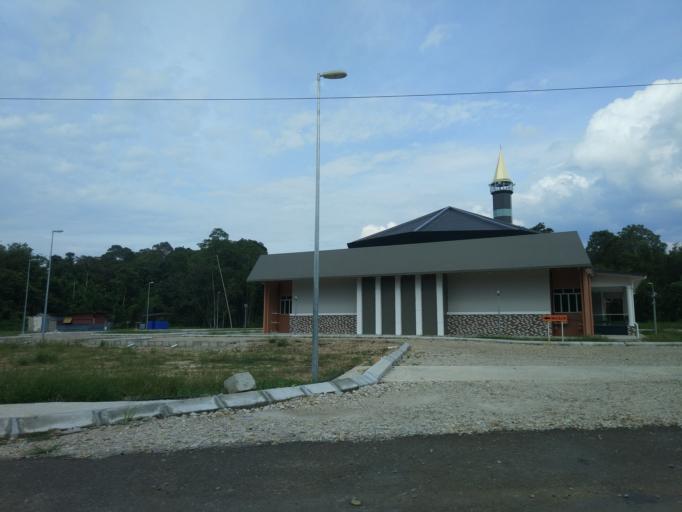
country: MY
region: Sabah
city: Bandar Labuan
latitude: 4.9592
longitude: 115.5059
